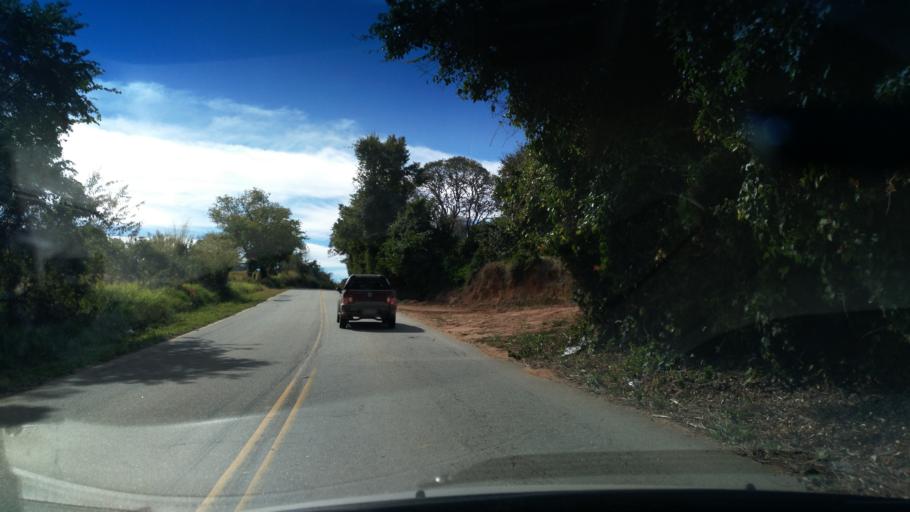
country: BR
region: Minas Gerais
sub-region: Andradas
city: Andradas
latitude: -22.0686
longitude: -46.4538
